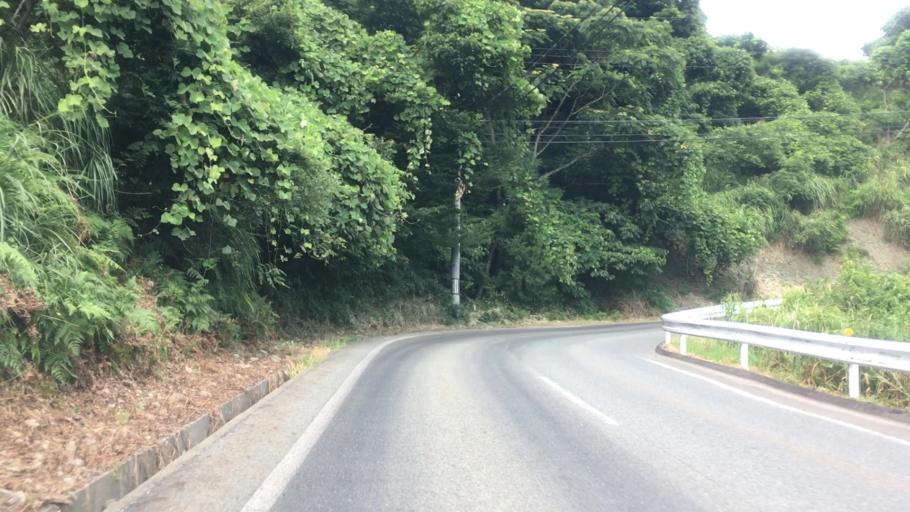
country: JP
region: Hyogo
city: Toyooka
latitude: 35.5149
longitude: 134.7822
